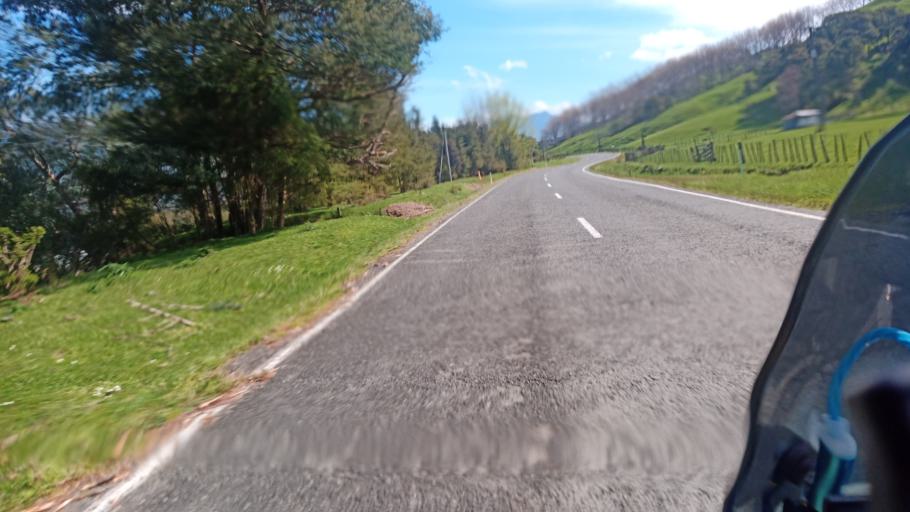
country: NZ
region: Gisborne
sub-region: Gisborne District
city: Gisborne
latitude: -37.8641
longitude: 178.2341
